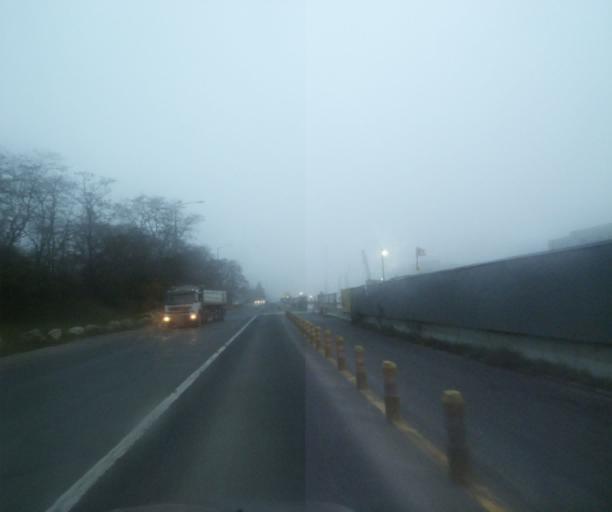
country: FR
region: Ile-de-France
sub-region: Departement de Seine-Saint-Denis
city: Noisy-le-Grand
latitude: 48.8412
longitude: 2.5810
